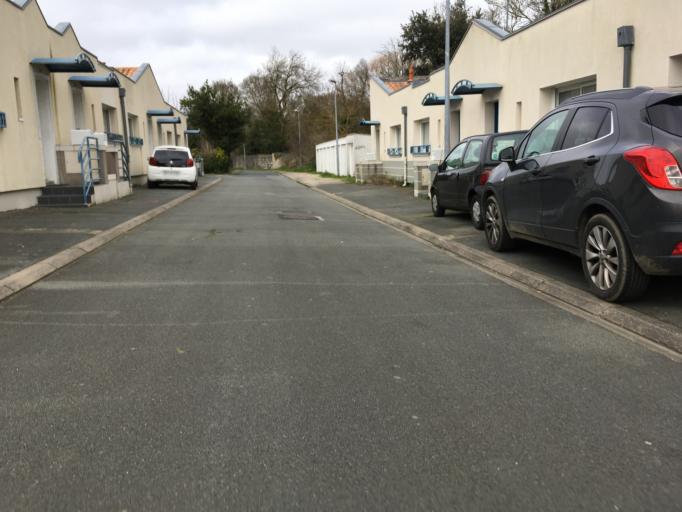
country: FR
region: Poitou-Charentes
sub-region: Departement de la Charente-Maritime
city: La Rochelle
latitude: 46.1765
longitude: -1.1449
